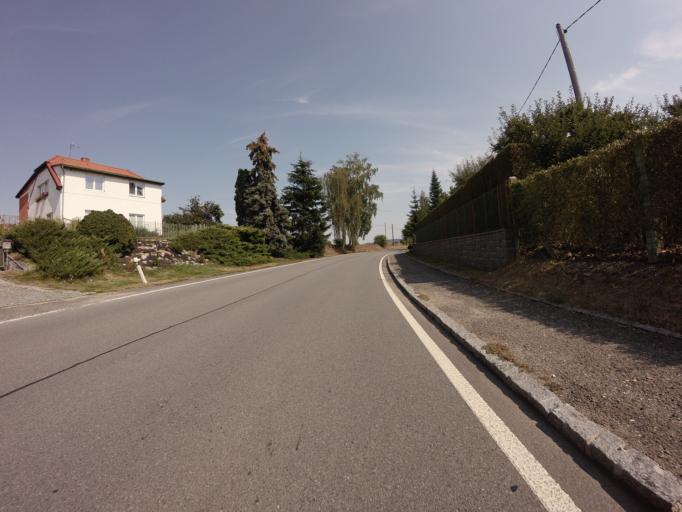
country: CZ
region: Central Bohemia
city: Sedlcany
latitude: 49.6288
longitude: 14.4254
